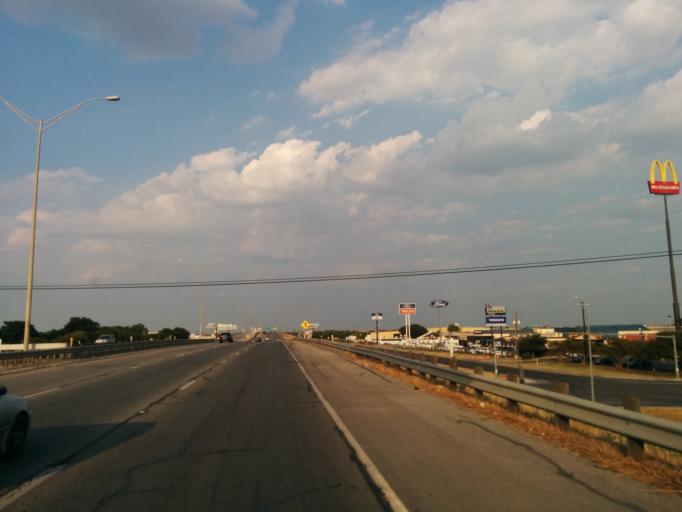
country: US
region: Texas
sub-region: Bexar County
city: Kirby
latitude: 29.4313
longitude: -98.4065
